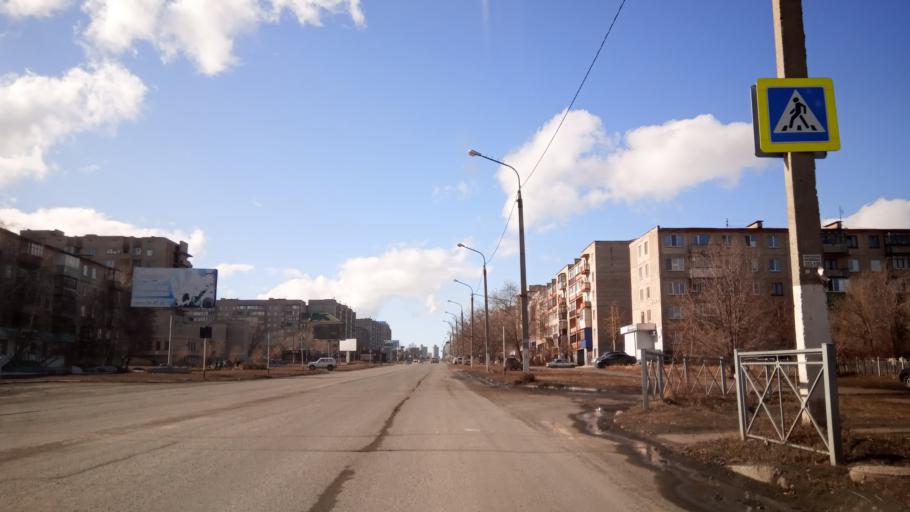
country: RU
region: Orenburg
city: Novotroitsk
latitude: 51.1845
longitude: 58.2807
